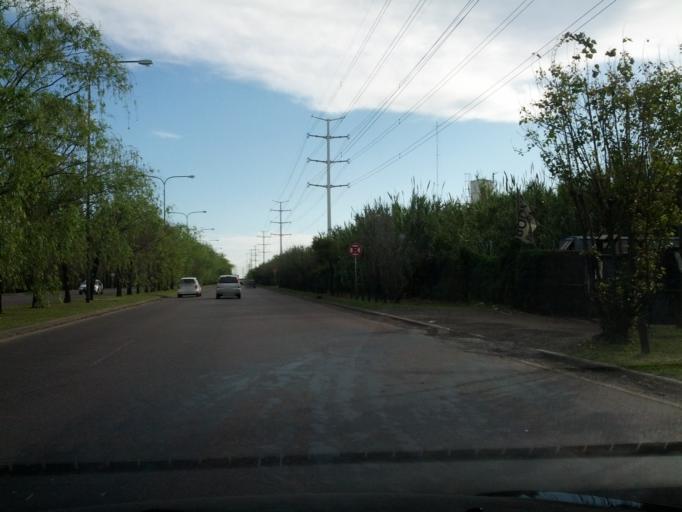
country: AR
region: Buenos Aires F.D.
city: Villa Lugano
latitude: -34.6956
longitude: -58.4536
